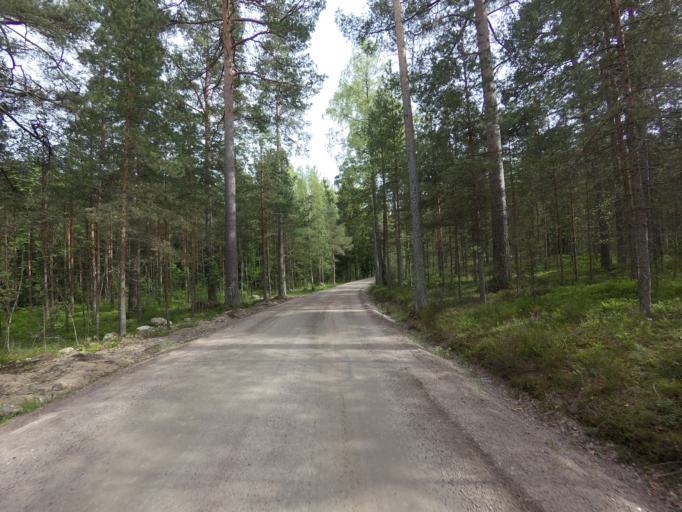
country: FI
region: Uusimaa
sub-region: Helsinki
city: Koukkuniemi
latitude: 60.1312
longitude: 24.6967
